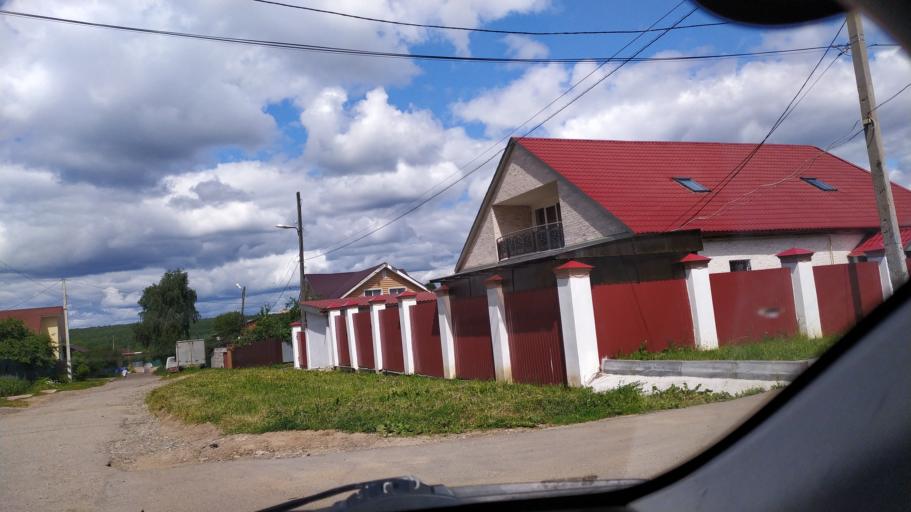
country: RU
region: Chuvashia
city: Novyye Lapsary
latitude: 56.1115
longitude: 47.1775
